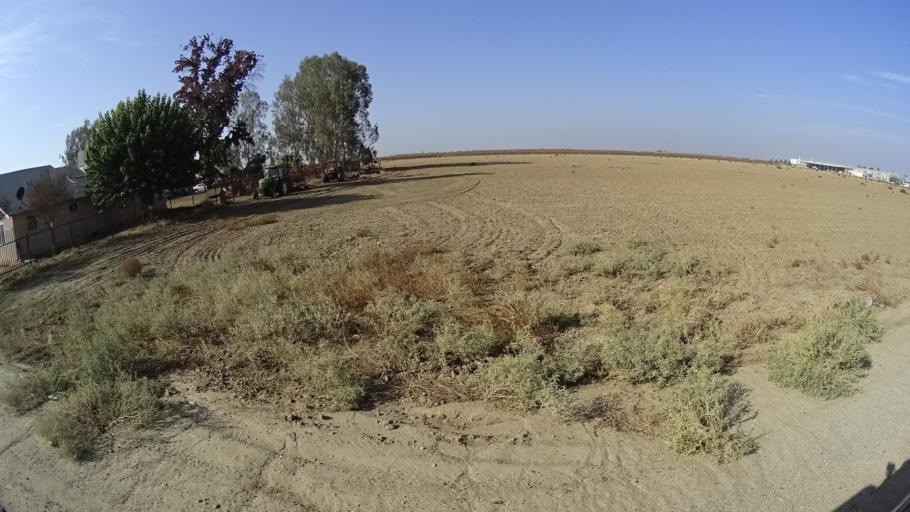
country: US
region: California
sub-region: Kern County
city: McFarland
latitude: 35.6974
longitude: -119.2230
